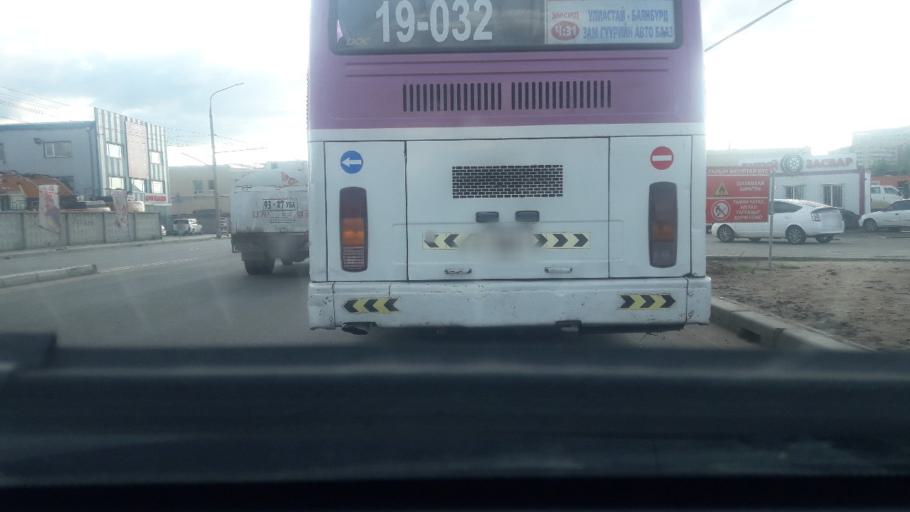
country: MN
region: Ulaanbaatar
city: Ulaanbaatar
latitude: 47.9125
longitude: 106.9838
